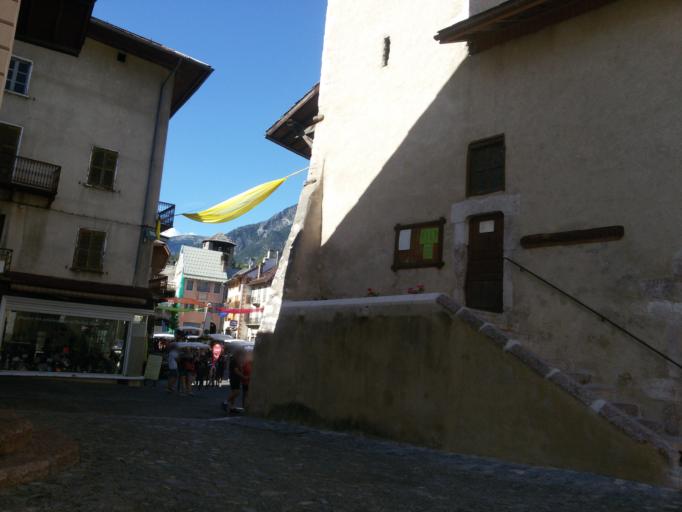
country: FR
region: Provence-Alpes-Cote d'Azur
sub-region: Departement des Hautes-Alpes
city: Guillestre
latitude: 44.6594
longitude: 6.6493
